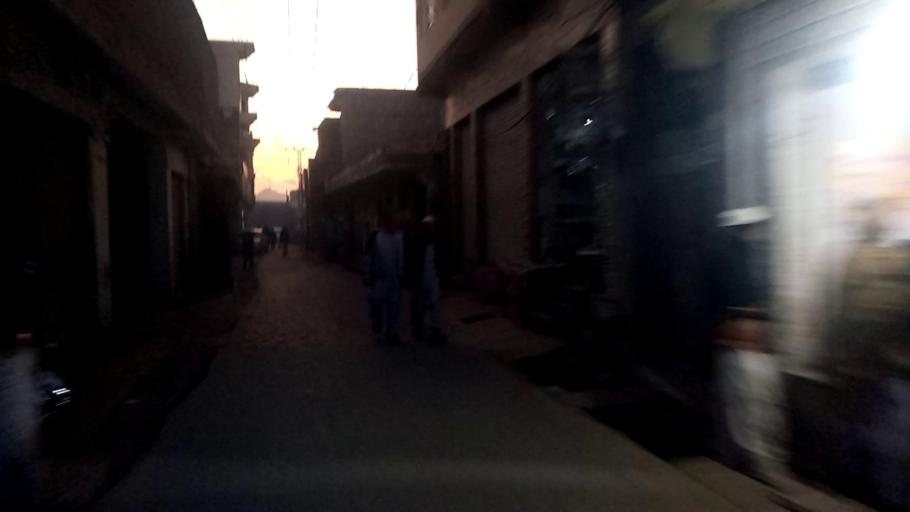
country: PK
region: Khyber Pakhtunkhwa
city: Mingora
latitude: 34.7780
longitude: 72.3555
